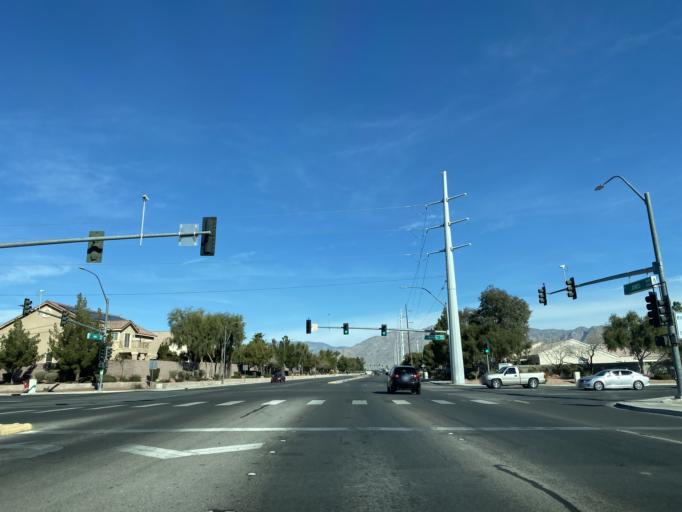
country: US
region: Nevada
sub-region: Clark County
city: North Las Vegas
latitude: 36.2680
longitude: -115.2253
